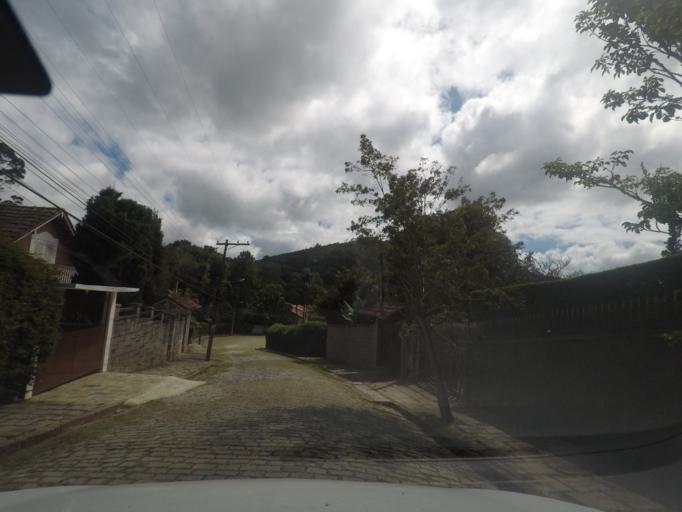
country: BR
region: Rio de Janeiro
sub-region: Teresopolis
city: Teresopolis
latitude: -22.3964
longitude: -42.9869
